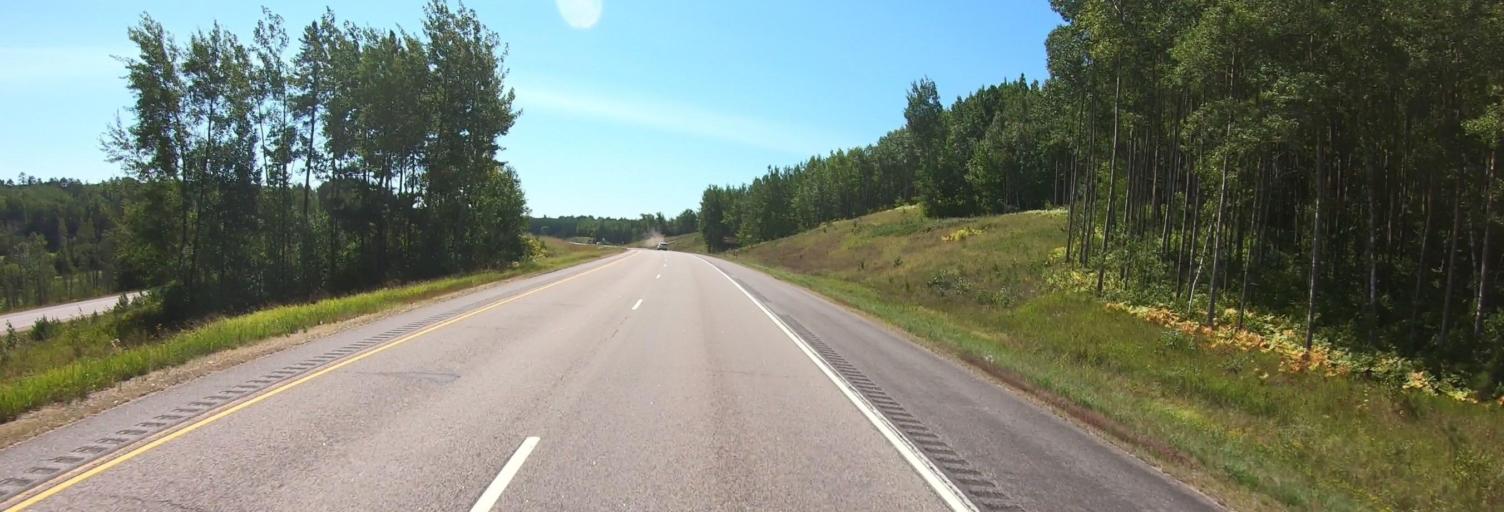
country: US
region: Minnesota
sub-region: Saint Louis County
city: Mountain Iron
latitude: 47.6803
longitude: -92.6532
